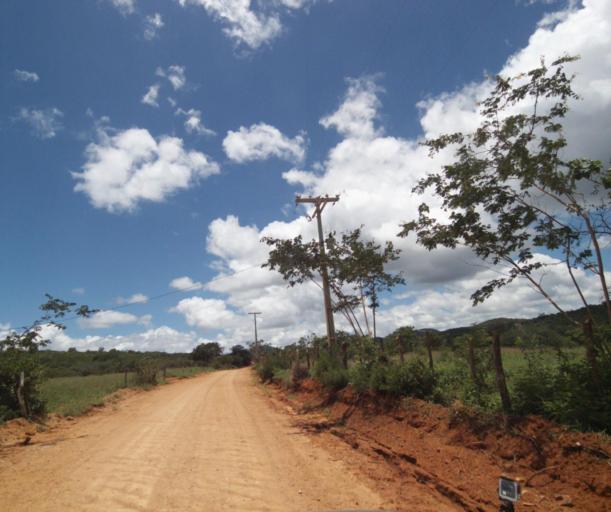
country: BR
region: Bahia
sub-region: Pocoes
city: Pocoes
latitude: -14.3791
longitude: -40.3950
